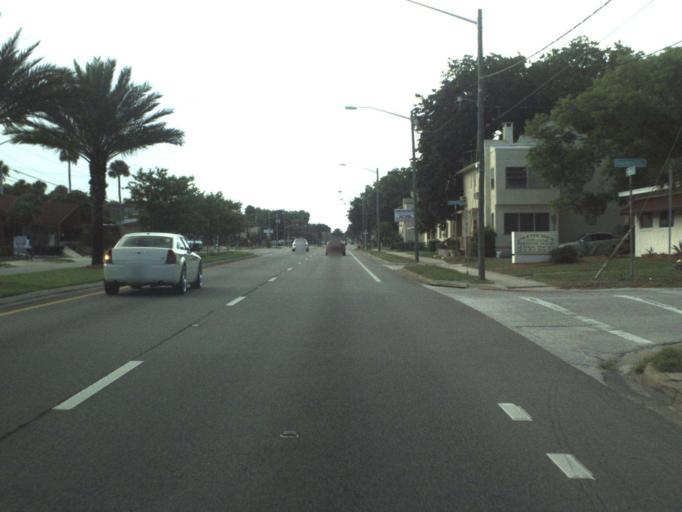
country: US
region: Florida
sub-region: Volusia County
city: Daytona Beach
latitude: 29.1906
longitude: -81.0118
